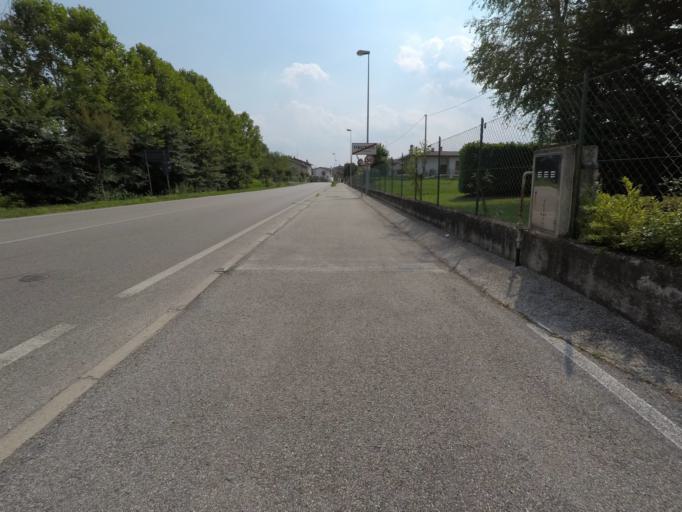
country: IT
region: Friuli Venezia Giulia
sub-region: Provincia di Pordenone
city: Caneva
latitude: 45.9788
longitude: 12.4727
